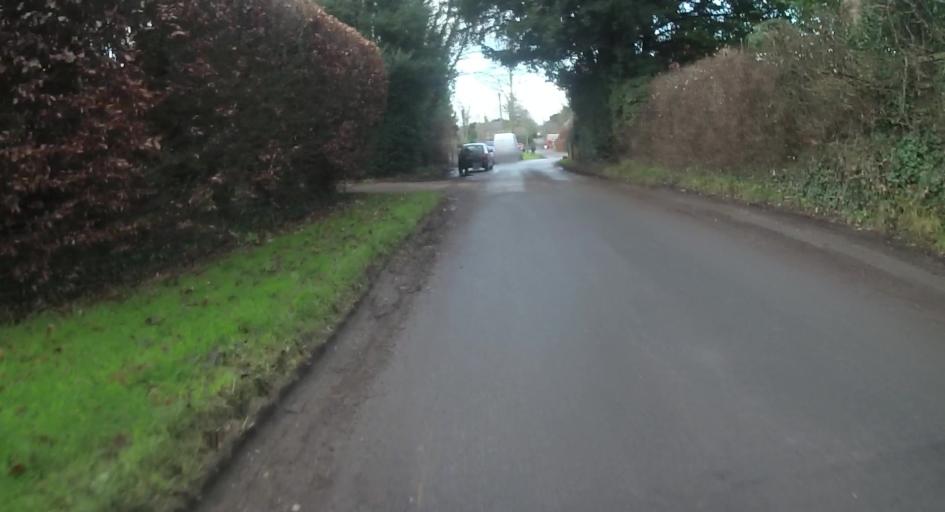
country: GB
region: England
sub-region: Hampshire
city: Basingstoke
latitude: 51.2747
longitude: -1.1518
